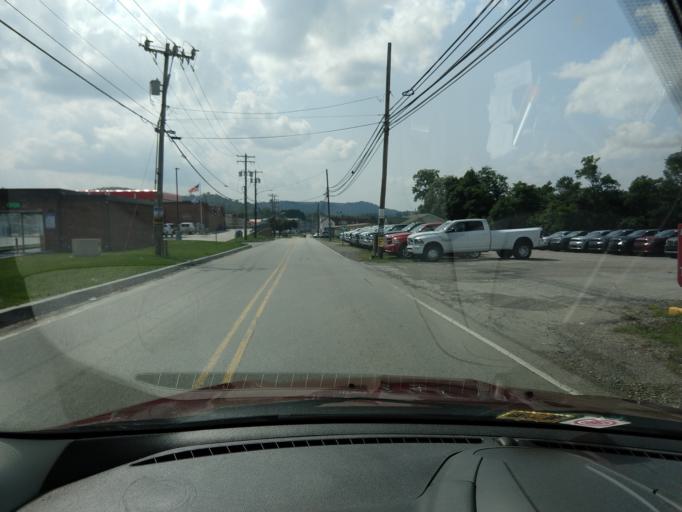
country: US
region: Pennsylvania
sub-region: Greene County
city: Morrisville
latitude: 39.8971
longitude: -80.1614
